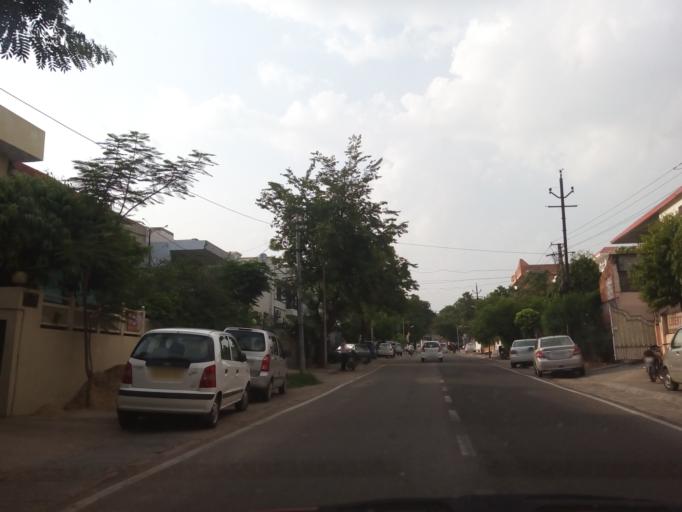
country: IN
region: Rajasthan
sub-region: Jaipur
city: Jaipur
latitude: 26.9156
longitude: 75.7951
